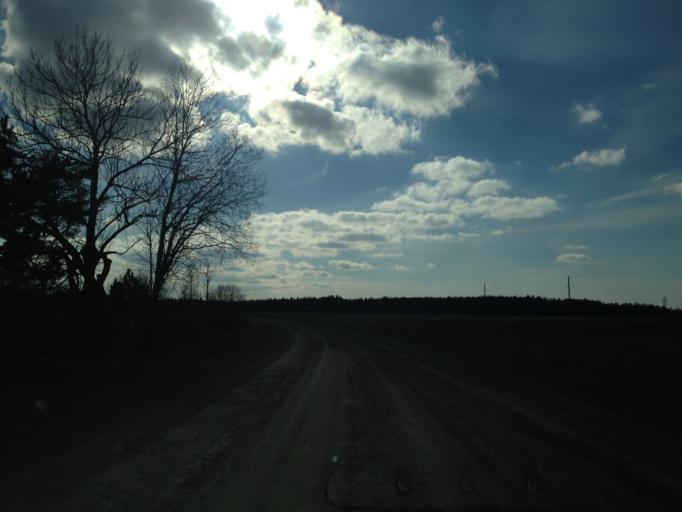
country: EE
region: Harju
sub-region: Nissi vald
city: Riisipere
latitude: 59.1250
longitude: 24.3657
